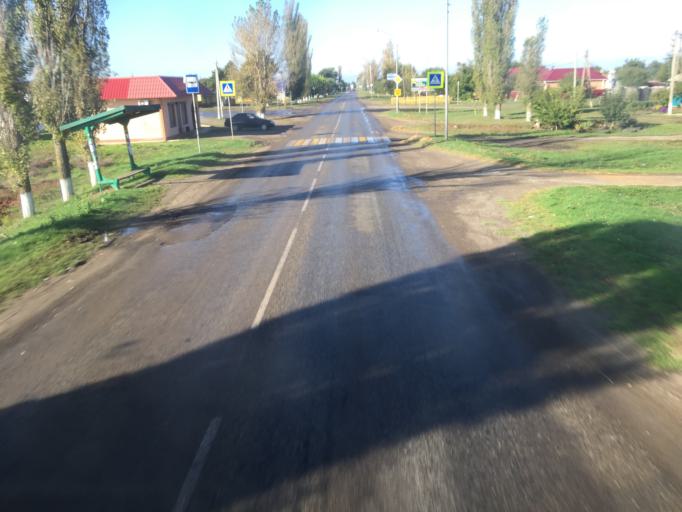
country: RU
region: Rostov
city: Peschanokopskoye
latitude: 46.1932
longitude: 41.1009
